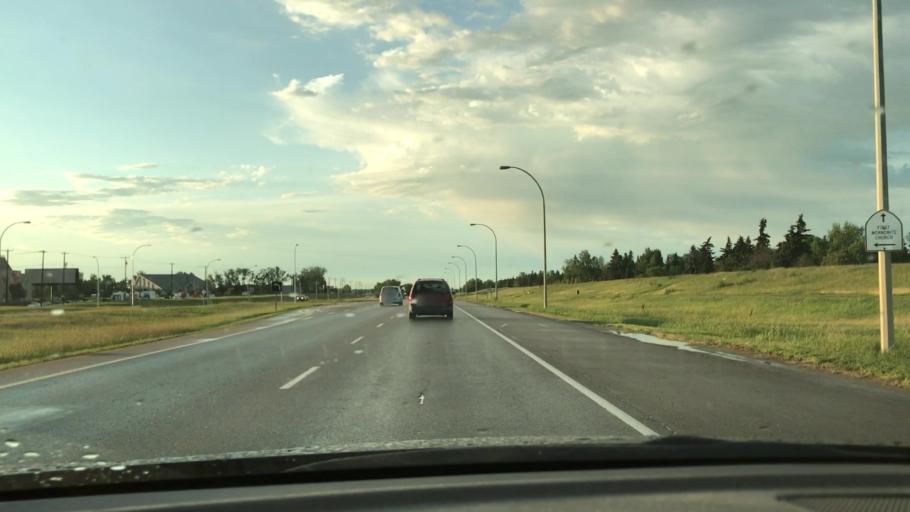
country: CA
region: Alberta
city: Edmonton
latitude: 53.4672
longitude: -113.4663
